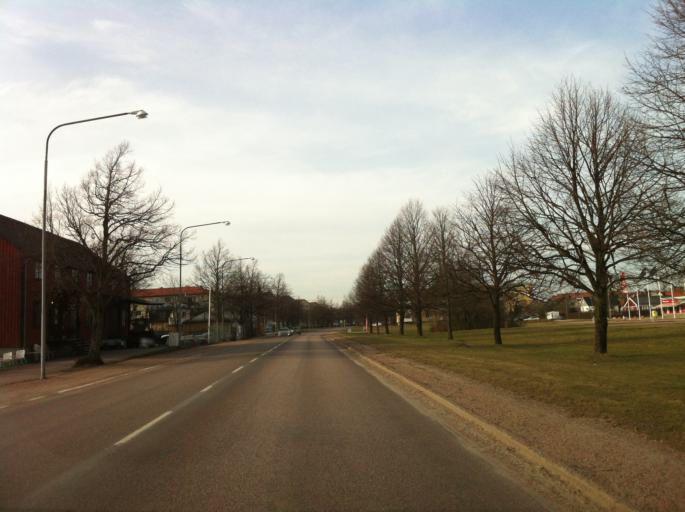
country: SE
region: Vaermland
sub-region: Kristinehamns Kommun
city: Kristinehamn
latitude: 59.2989
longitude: 14.1175
